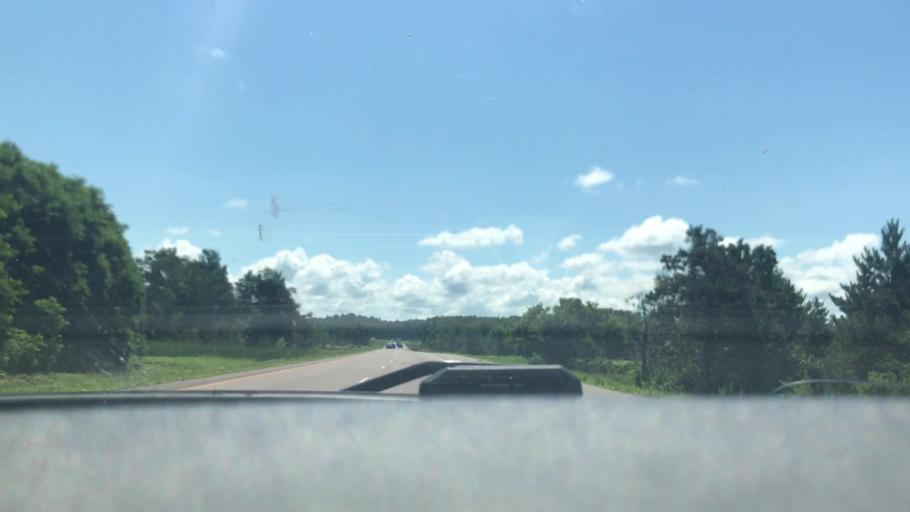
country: US
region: Wisconsin
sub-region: Trempealeau County
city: Osseo
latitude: 44.5211
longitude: -91.1453
